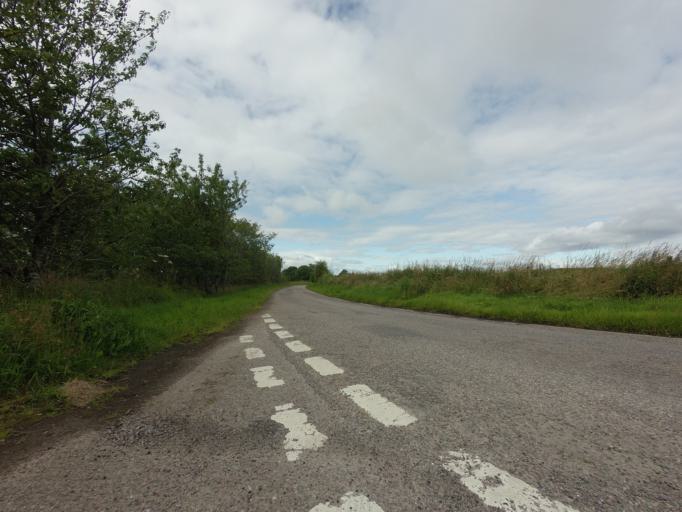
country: GB
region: Scotland
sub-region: Moray
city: Elgin
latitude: 57.6712
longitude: -3.3845
